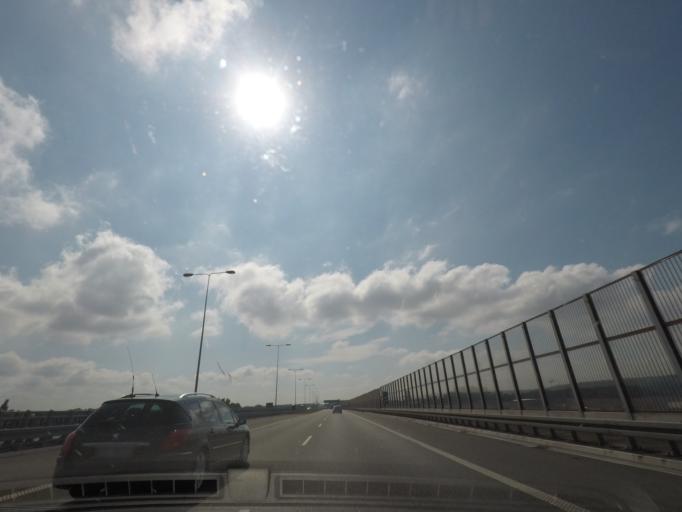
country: PL
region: Kujawsko-Pomorskie
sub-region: Powiat aleksandrowski
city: Ciechocinek
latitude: 52.8713
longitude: 18.7532
